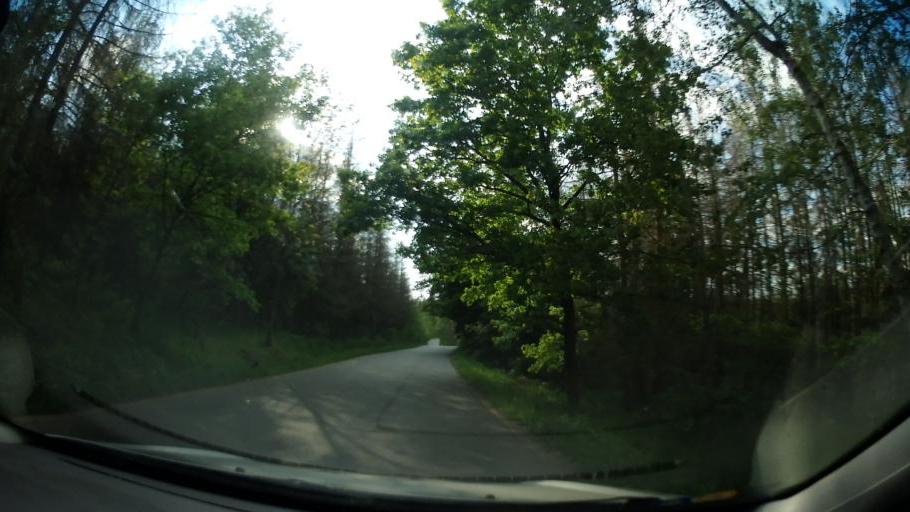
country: CZ
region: Vysocina
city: Budisov
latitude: 49.2811
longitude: 16.0001
